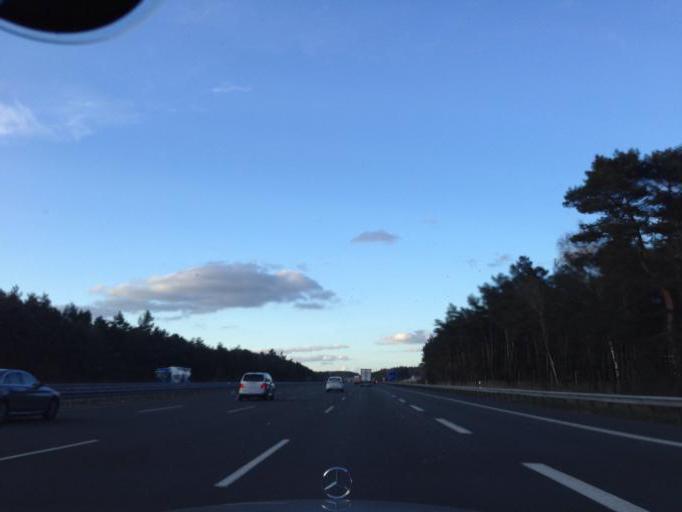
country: DE
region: Lower Saxony
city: Hademstorf
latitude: 52.7761
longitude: 9.6686
